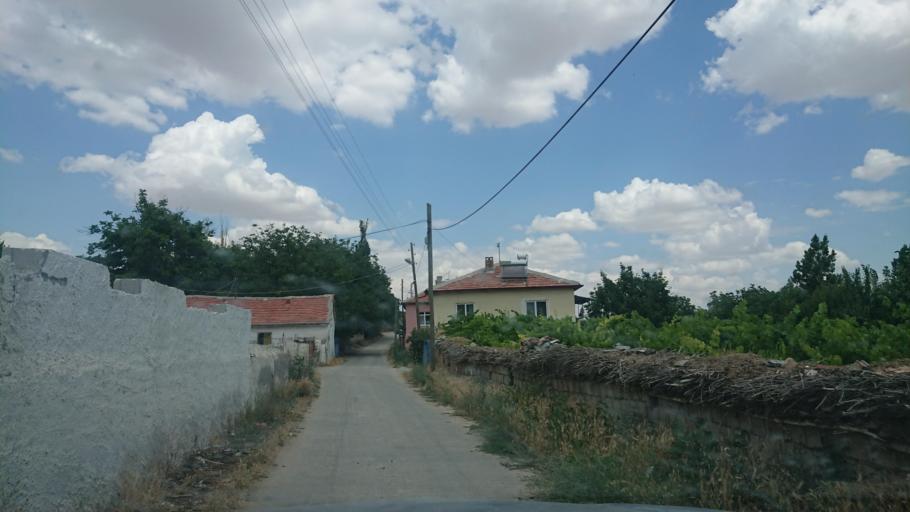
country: TR
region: Aksaray
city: Agacoren
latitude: 38.8873
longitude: 33.8801
